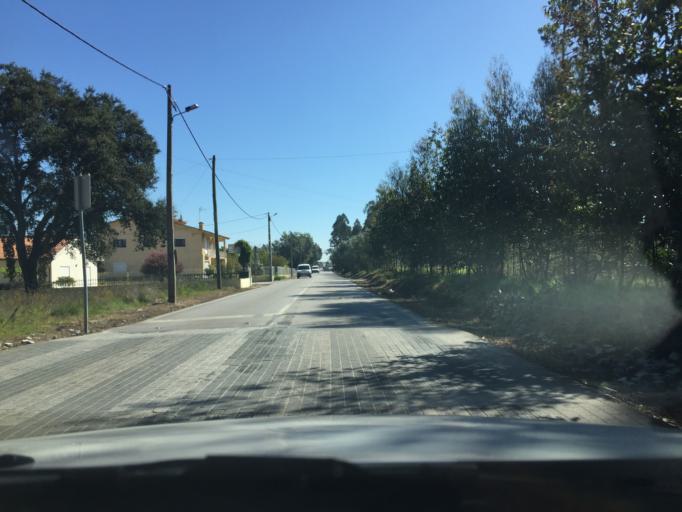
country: PT
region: Coimbra
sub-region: Cantanhede
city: Cantanhede
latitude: 40.4200
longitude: -8.5468
